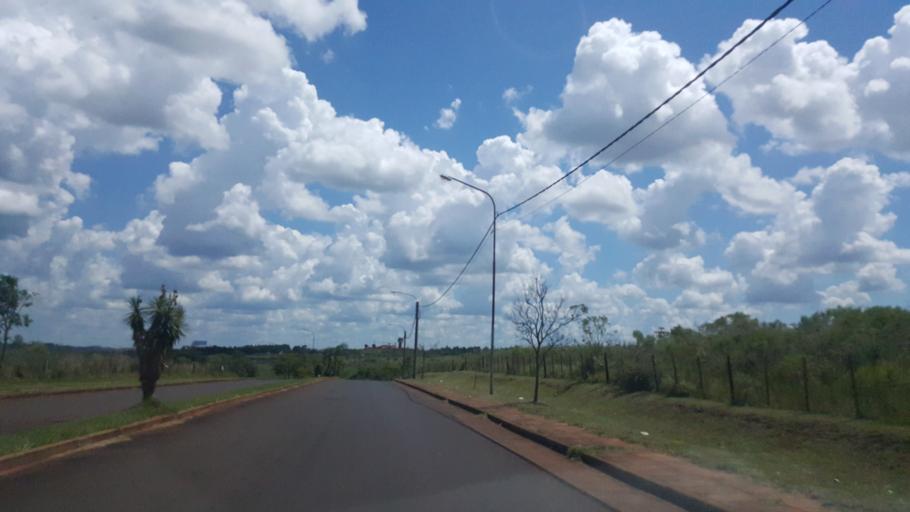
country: AR
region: Misiones
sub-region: Departamento de Capital
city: Posadas
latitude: -27.3805
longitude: -55.9627
